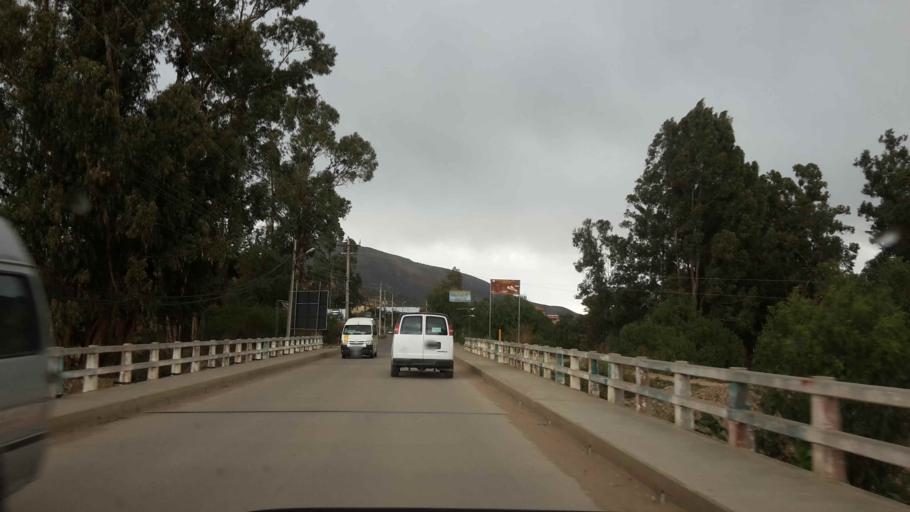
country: BO
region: Cochabamba
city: Tarata
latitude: -17.6093
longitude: -66.0252
